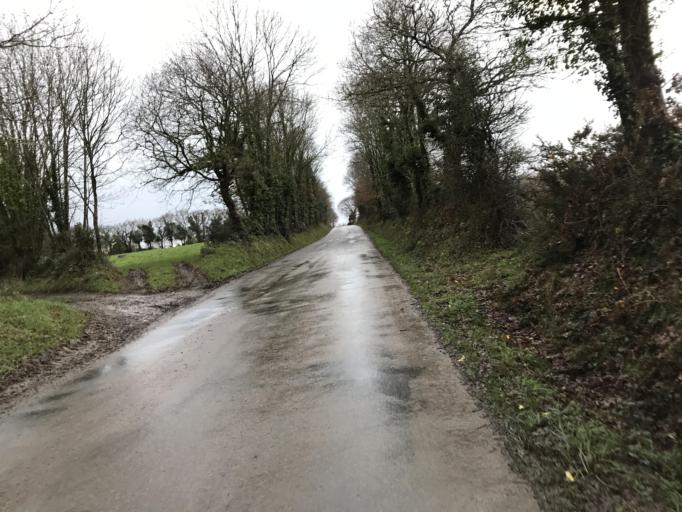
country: FR
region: Brittany
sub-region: Departement du Finistere
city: Loperhet
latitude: 48.3640
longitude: -4.3255
